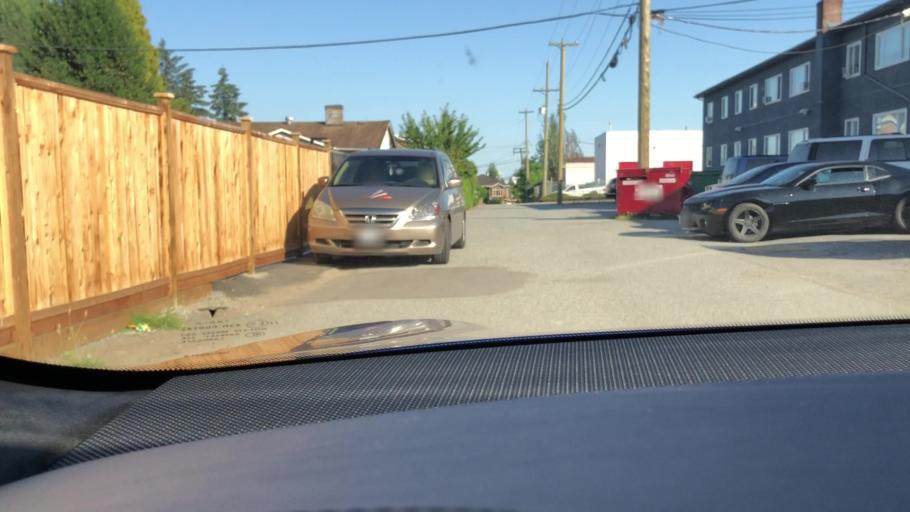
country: CA
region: British Columbia
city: New Westminster
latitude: 49.2256
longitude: -122.9344
